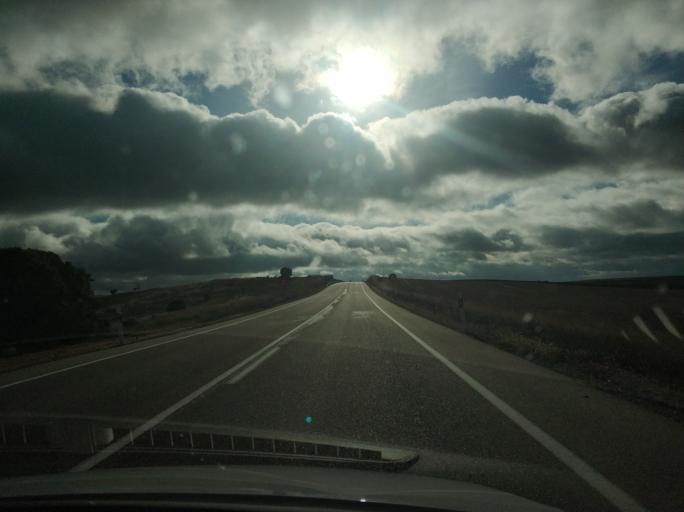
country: ES
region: Castille and Leon
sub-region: Provincia de Soria
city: Fuentecambron
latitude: 41.4681
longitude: -3.3262
